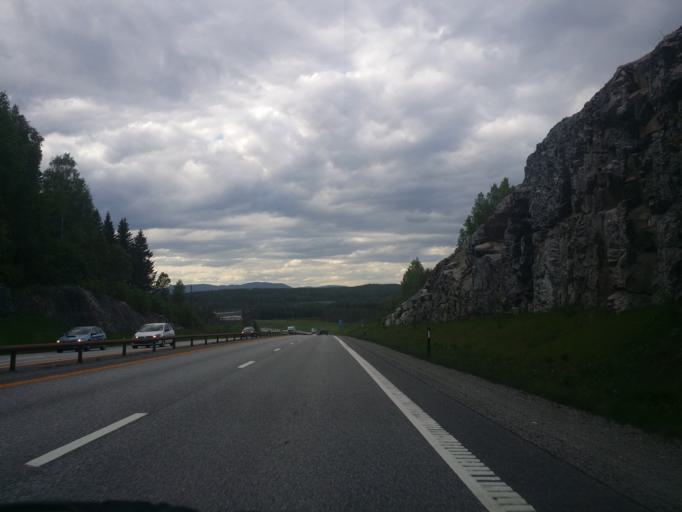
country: NO
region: Akershus
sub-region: Eidsvoll
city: Raholt
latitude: 60.2758
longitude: 11.1494
